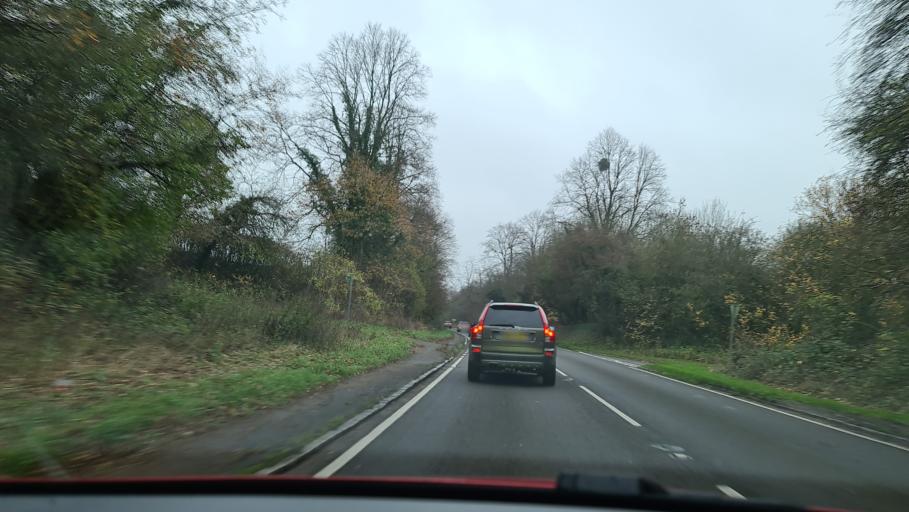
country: GB
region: England
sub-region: Buckinghamshire
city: Stokenchurch
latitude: 51.6402
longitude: -0.8260
